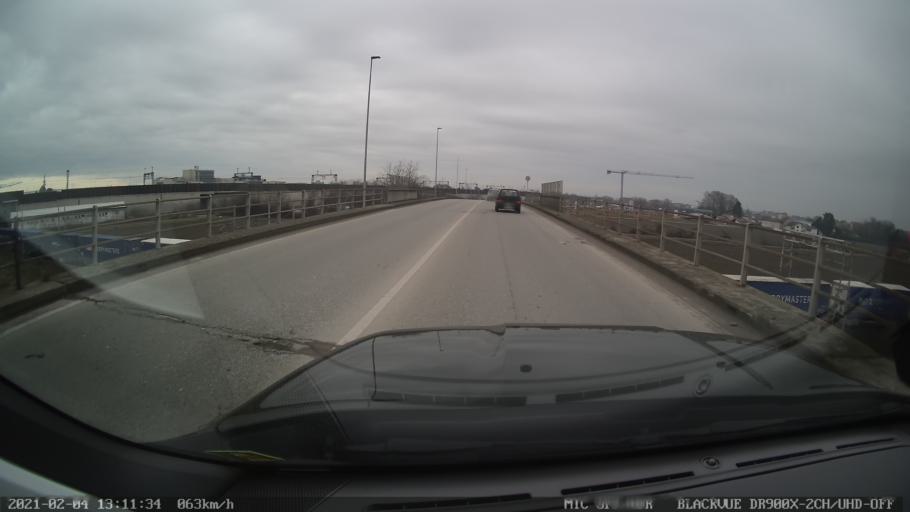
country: IT
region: Piedmont
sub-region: Provincia di Novara
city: Novara
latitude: 45.4689
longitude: 8.6153
